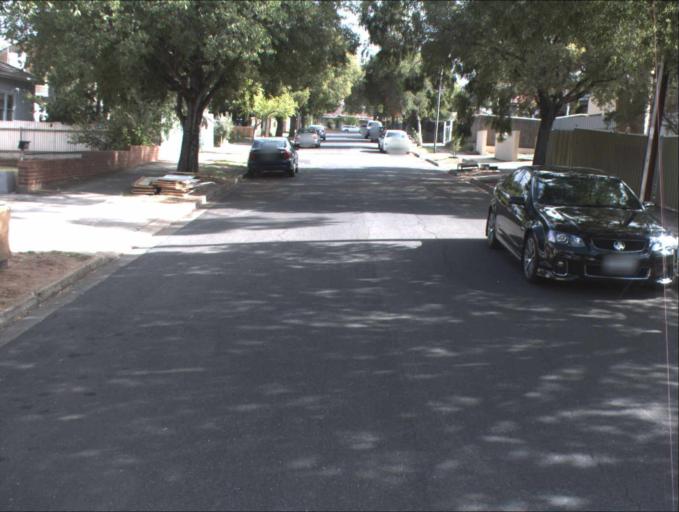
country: AU
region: South Australia
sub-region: Port Adelaide Enfield
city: Blair Athol
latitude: -34.8678
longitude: 138.6001
